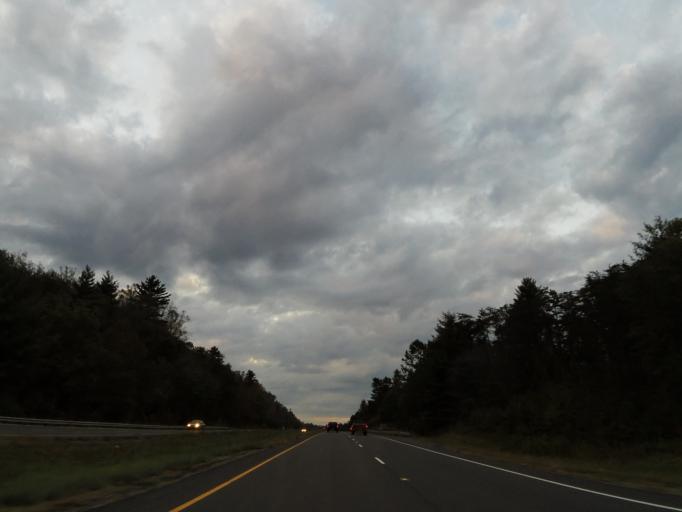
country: US
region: North Carolina
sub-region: Buncombe County
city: Weaverville
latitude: 35.7245
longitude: -82.6050
